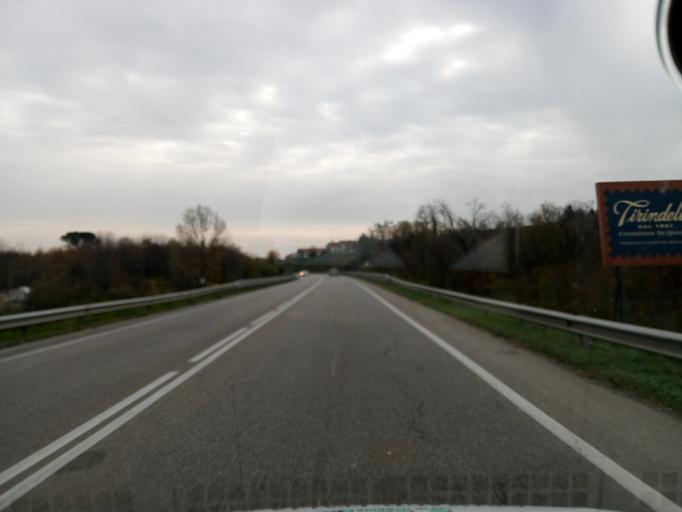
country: IT
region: Veneto
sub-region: Provincia di Treviso
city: Onigo
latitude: 45.8623
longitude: 11.9927
